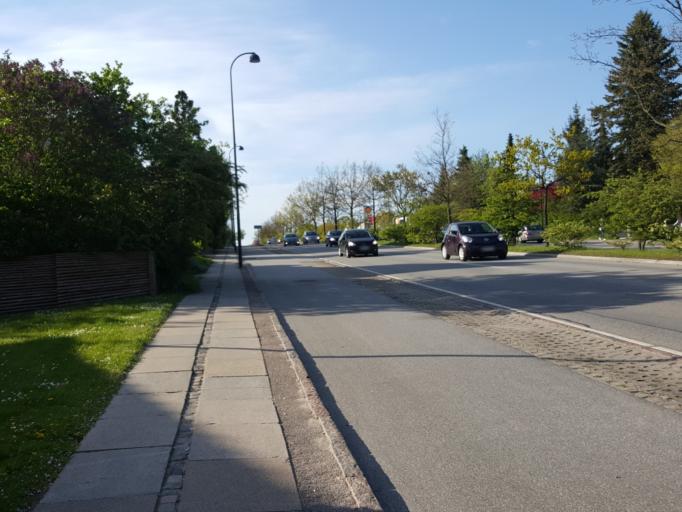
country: DK
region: Capital Region
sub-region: Rudersdal Kommune
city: Holte
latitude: 55.8172
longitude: 12.4684
